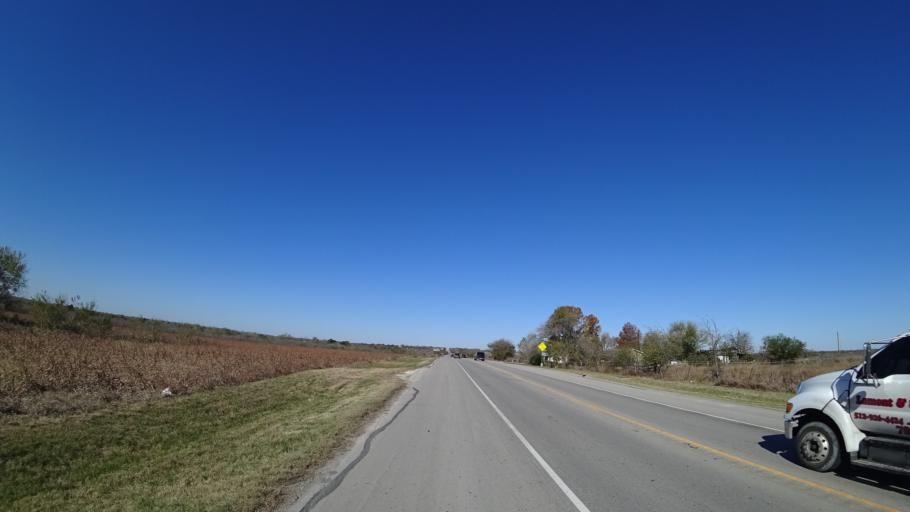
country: US
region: Texas
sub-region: Travis County
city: Garfield
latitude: 30.1104
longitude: -97.6233
